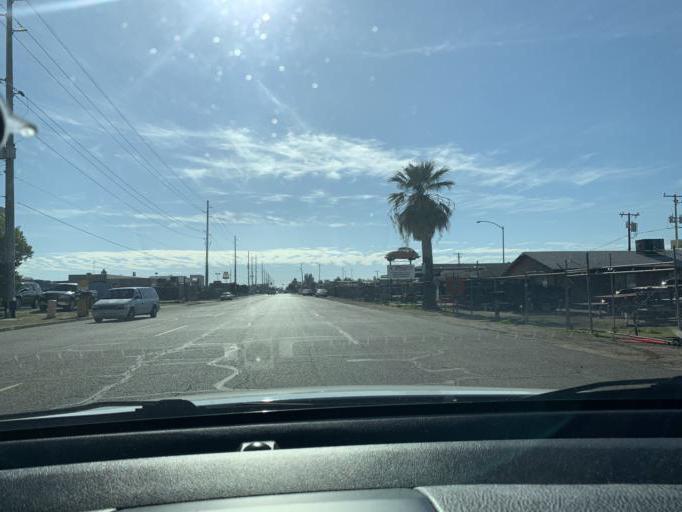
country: US
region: Arizona
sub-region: Maricopa County
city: Peoria
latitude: 33.6869
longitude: -112.1086
